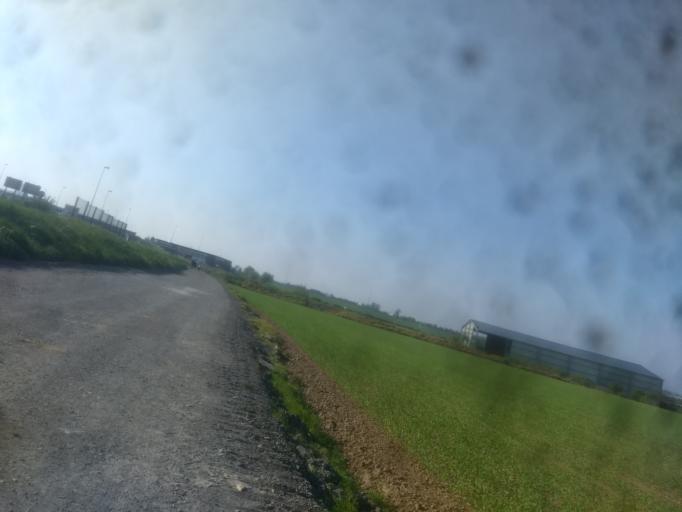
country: FR
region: Nord-Pas-de-Calais
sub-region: Departement du Pas-de-Calais
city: Beaurains
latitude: 50.2677
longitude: 2.8031
